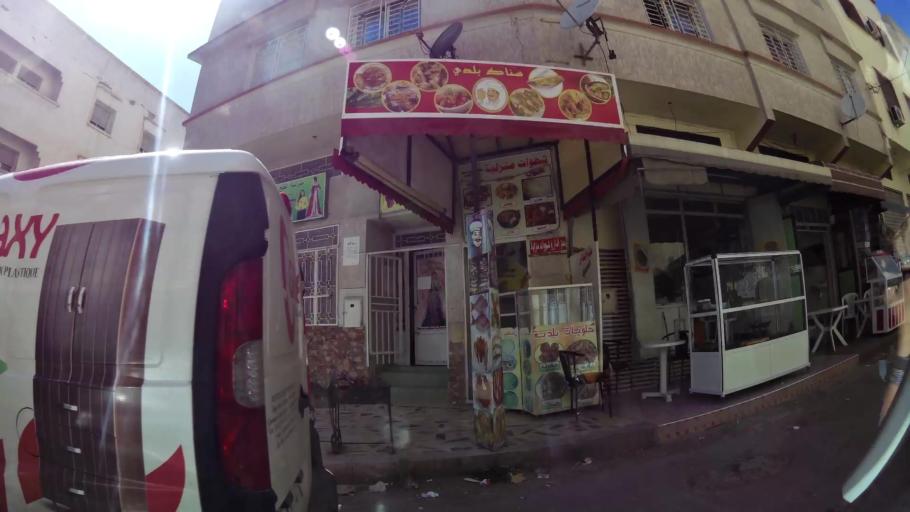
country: MA
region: Meknes-Tafilalet
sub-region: Meknes
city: Meknes
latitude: 33.8832
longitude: -5.5725
